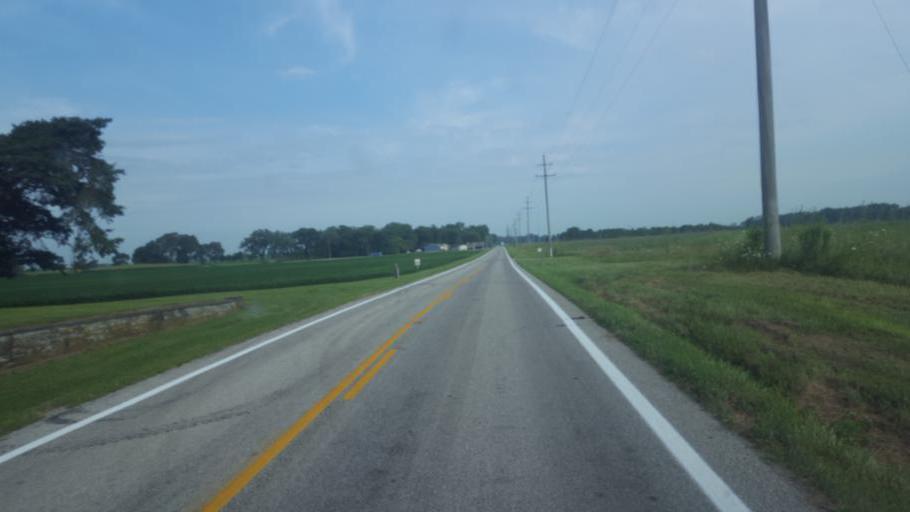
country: US
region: Ohio
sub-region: Marion County
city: Marion
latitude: 40.5516
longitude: -83.1943
